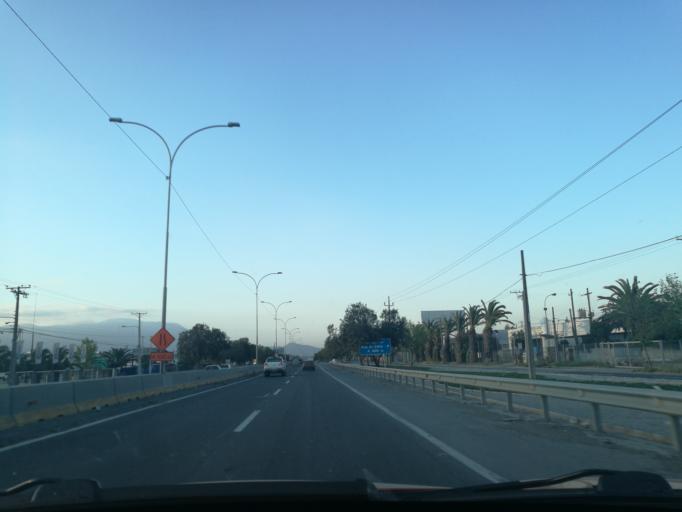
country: CL
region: O'Higgins
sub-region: Provincia de Cachapoal
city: Rancagua
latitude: -34.1640
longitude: -70.7274
